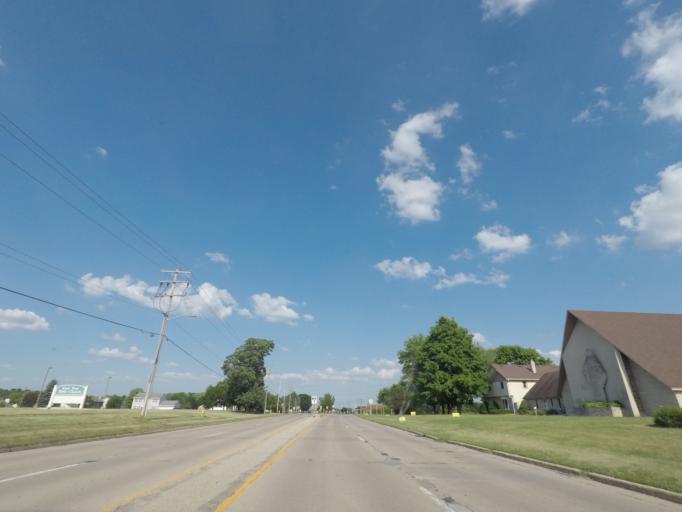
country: US
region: Wisconsin
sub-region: Walworth County
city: East Troy
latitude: 42.7923
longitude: -88.3969
